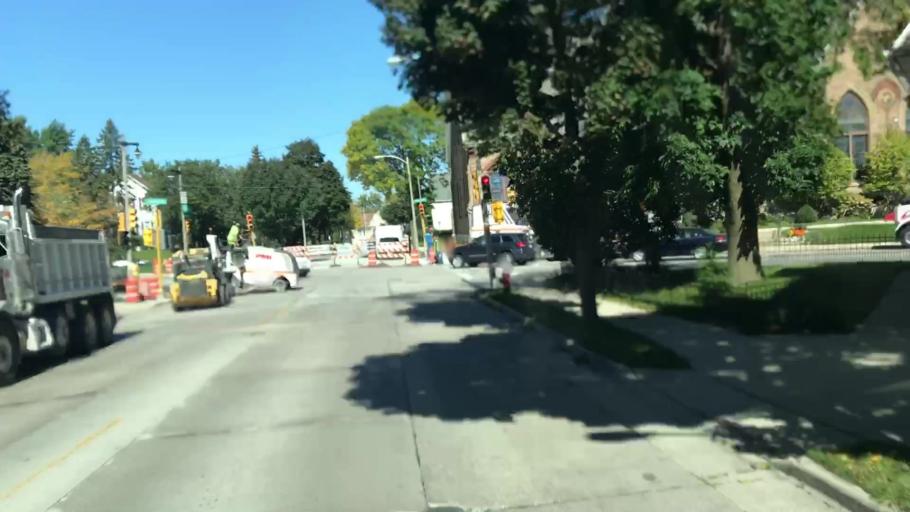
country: US
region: Wisconsin
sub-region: Milwaukee County
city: Saint Francis
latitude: 42.9942
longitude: -87.8942
